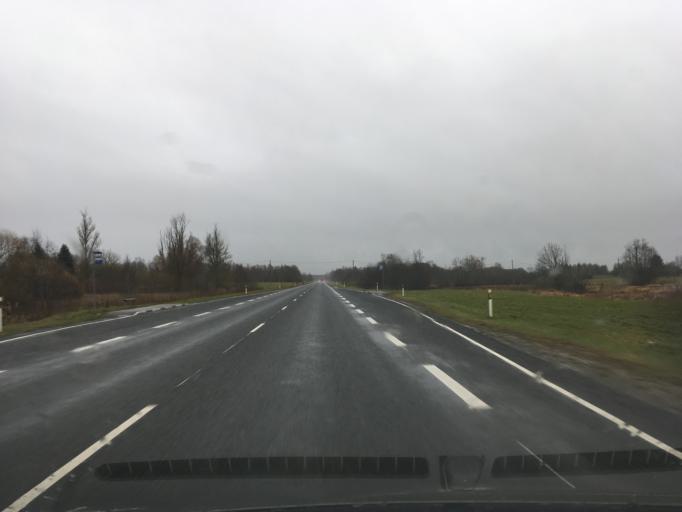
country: EE
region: Harju
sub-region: Nissi vald
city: Turba
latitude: 58.9184
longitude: 24.1126
